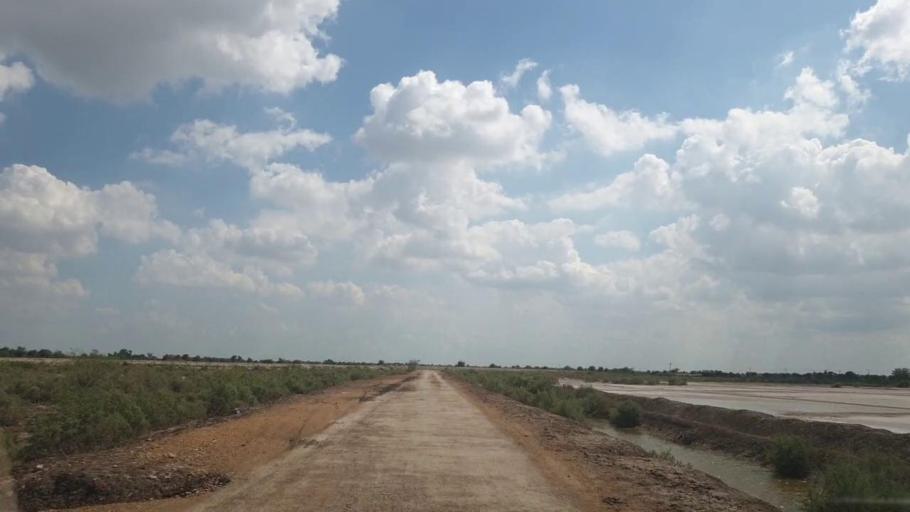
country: PK
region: Sindh
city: Pithoro
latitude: 25.5952
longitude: 69.4013
